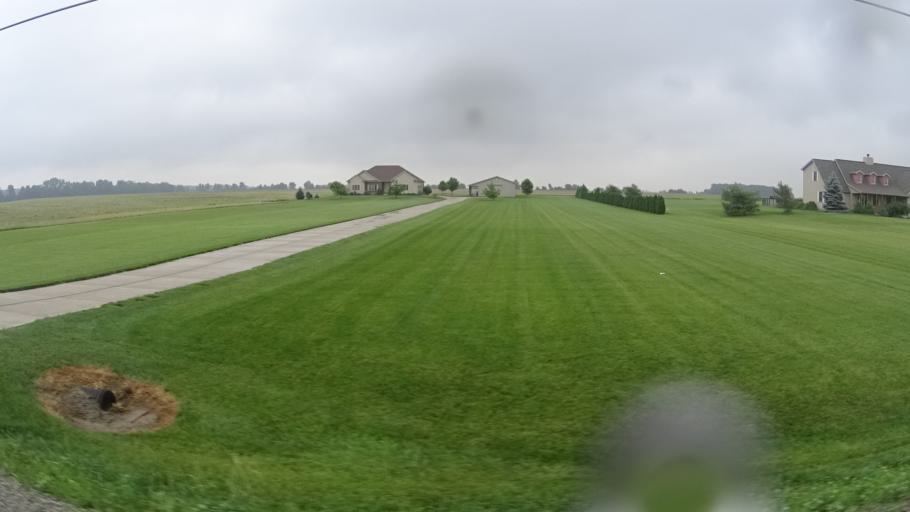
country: US
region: Ohio
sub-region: Huron County
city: Bellevue
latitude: 41.3175
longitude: -82.8296
